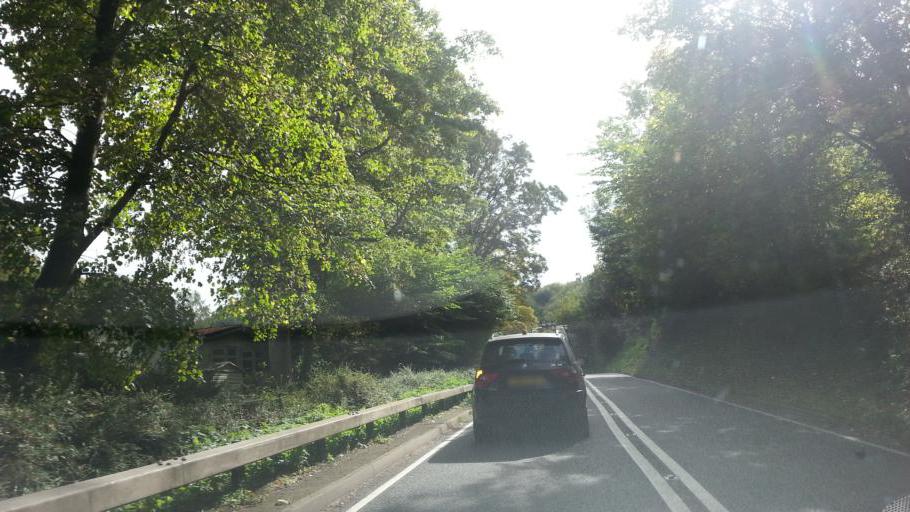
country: GB
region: England
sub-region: Gloucestershire
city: Mitcheldean
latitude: 51.8797
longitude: -2.4560
